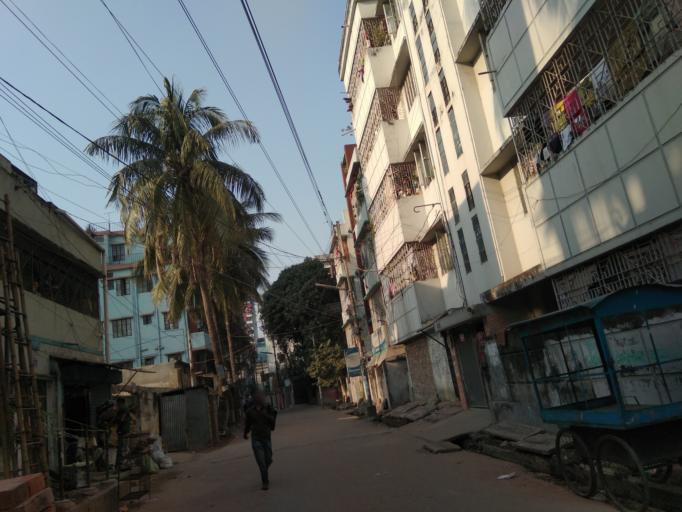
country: BD
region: Dhaka
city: Azimpur
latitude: 23.7721
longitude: 90.3632
